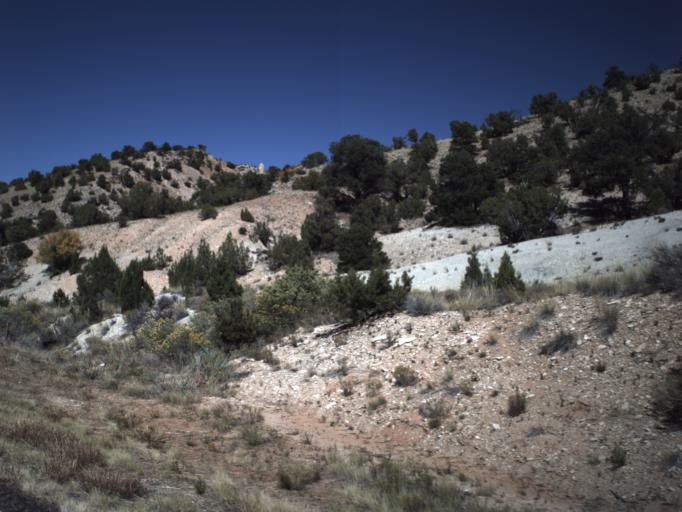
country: US
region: Utah
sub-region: Wayne County
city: Loa
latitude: 37.7552
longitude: -111.5699
